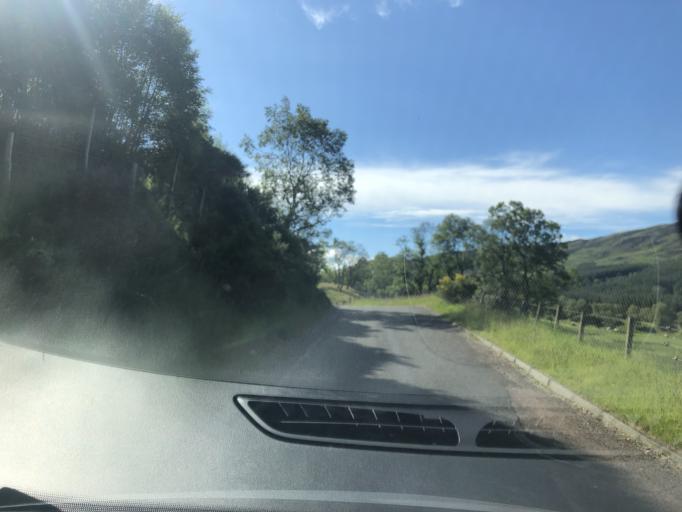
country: GB
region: Scotland
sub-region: Angus
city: Kirriemuir
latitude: 56.8379
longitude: -3.0868
